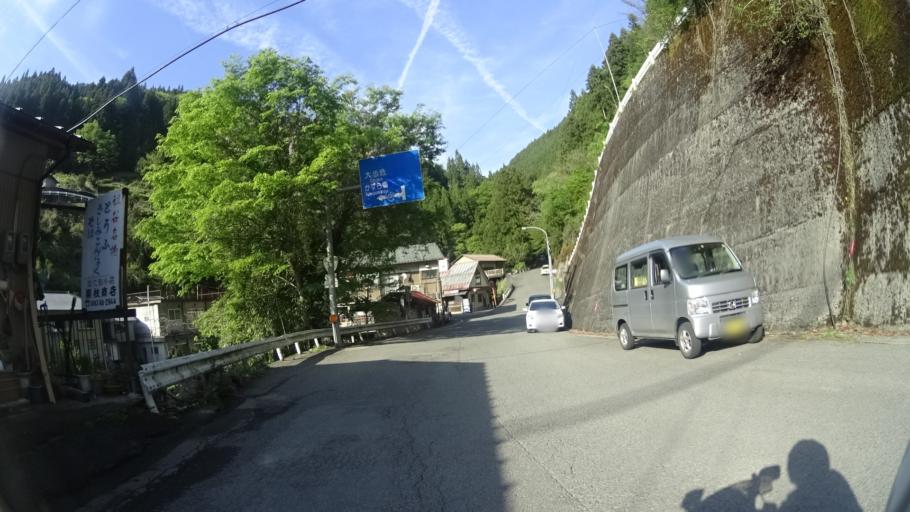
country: JP
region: Tokushima
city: Ikedacho
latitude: 33.8799
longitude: 133.9370
